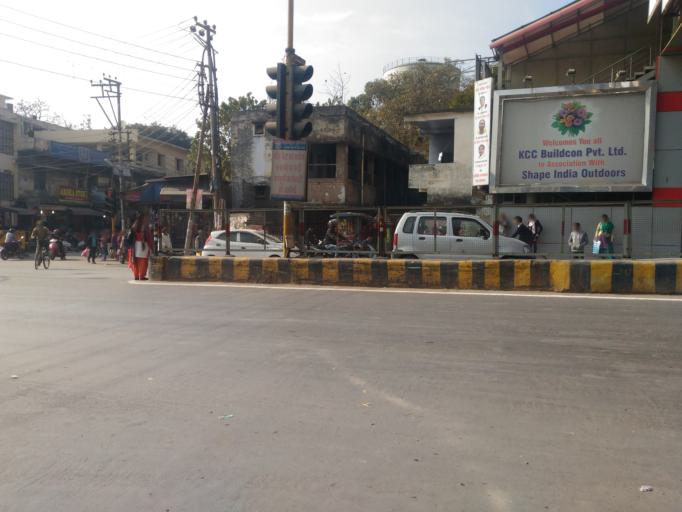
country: IN
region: Uttarakhand
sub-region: Dehradun
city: Dehradun
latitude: 30.3209
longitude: 78.0413
